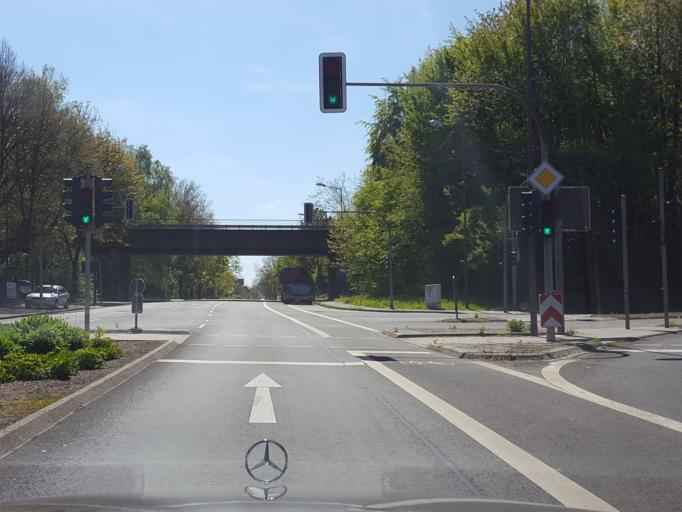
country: DE
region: North Rhine-Westphalia
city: Castrop-Rauxel
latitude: 51.5321
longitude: 7.3205
